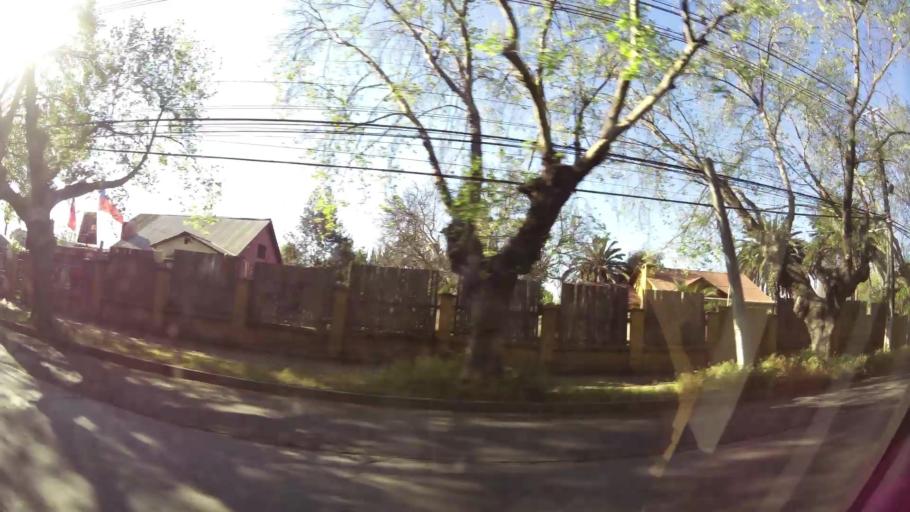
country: CL
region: Santiago Metropolitan
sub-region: Provincia de Talagante
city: Penaflor
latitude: -33.6101
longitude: -70.8645
